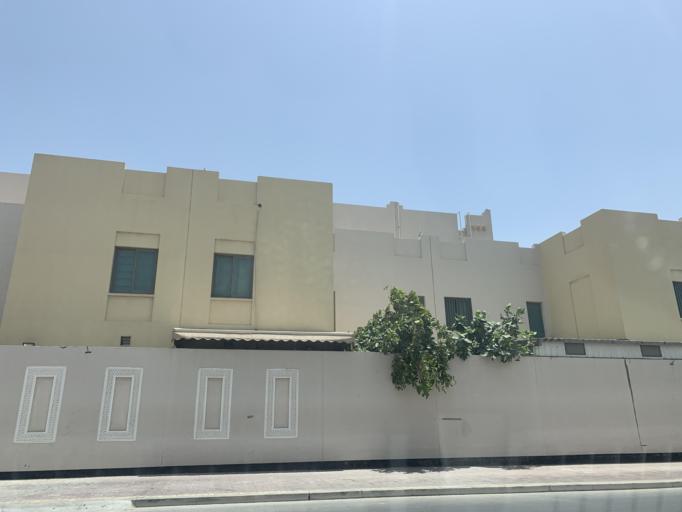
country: BH
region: Northern
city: Sitrah
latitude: 26.1627
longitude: 50.6265
